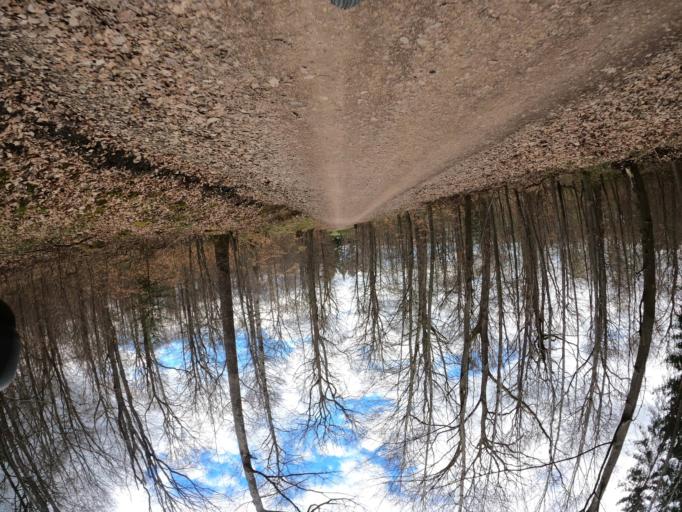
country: DE
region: Baden-Wuerttemberg
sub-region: Tuebingen Region
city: Wannweil
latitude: 48.4702
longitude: 9.1431
